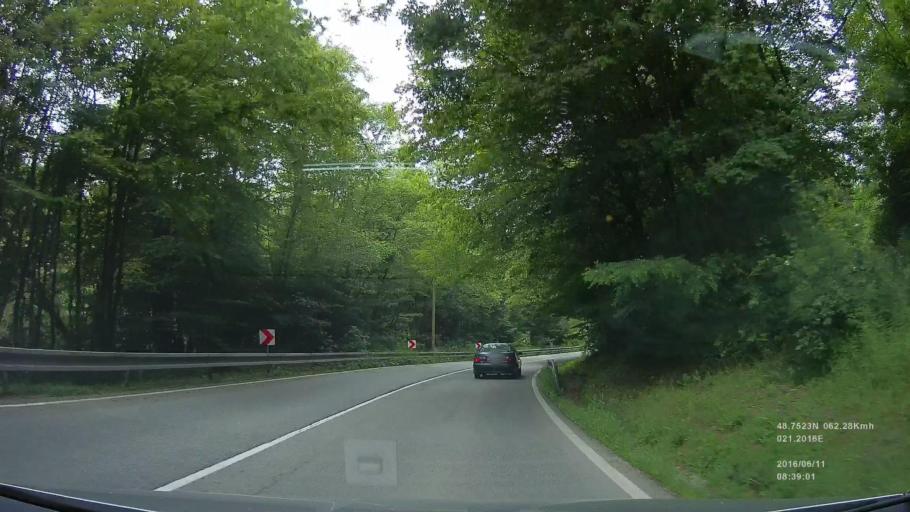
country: SK
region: Kosicky
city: Kosice
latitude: 48.7394
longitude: 21.2446
